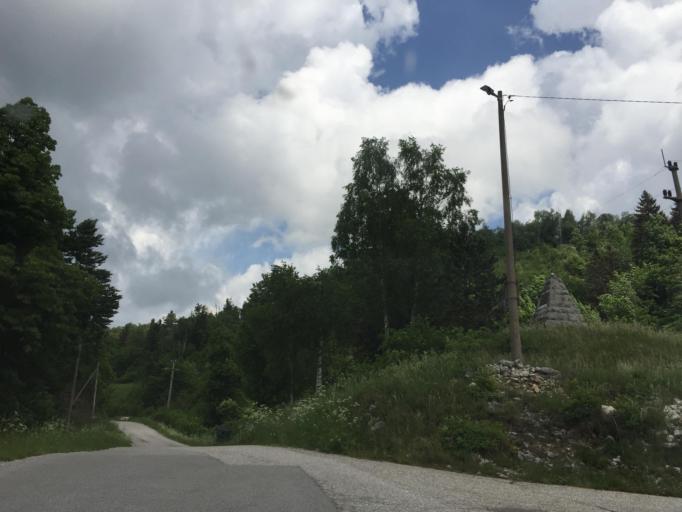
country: SI
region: Nova Gorica
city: Sempas
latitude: 46.0360
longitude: 13.7649
